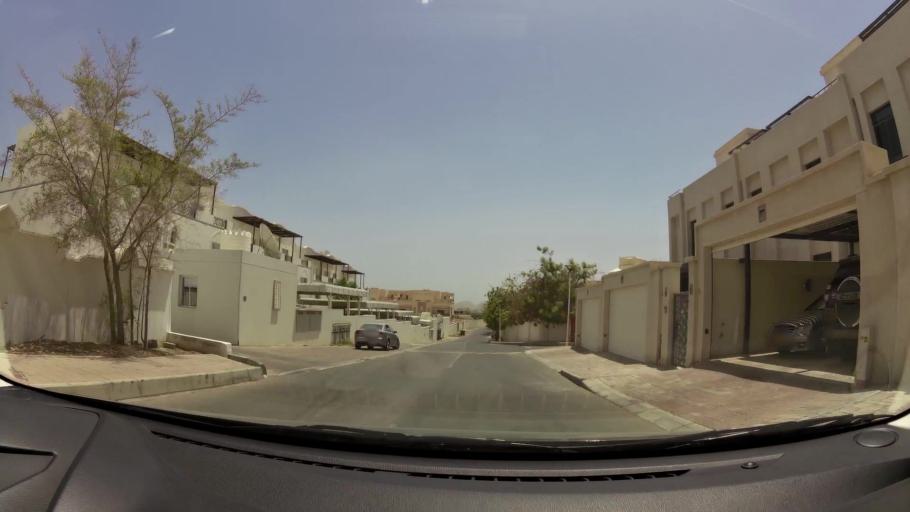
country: OM
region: Muhafazat Masqat
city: Bawshar
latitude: 23.6000
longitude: 58.4723
